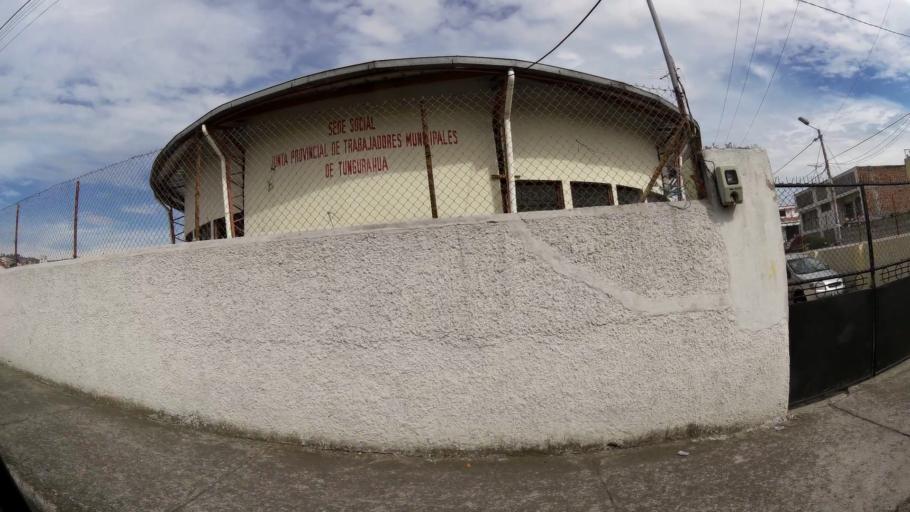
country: EC
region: Tungurahua
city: Ambato
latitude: -1.2494
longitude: -78.6306
